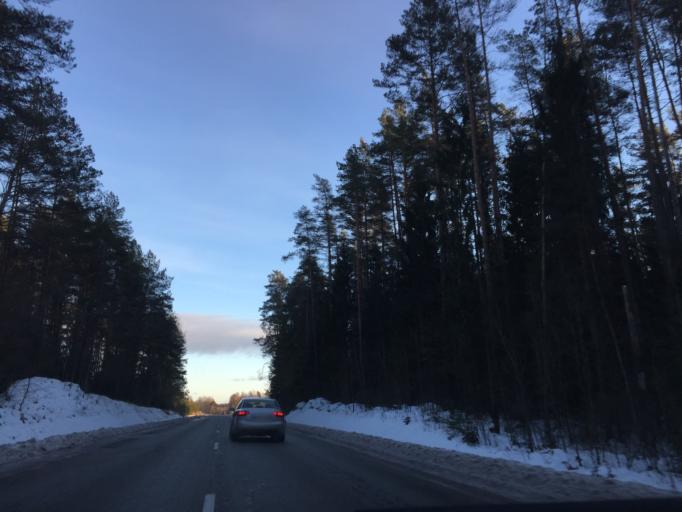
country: LV
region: Ogre
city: Jumprava
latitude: 56.6302
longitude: 24.9156
